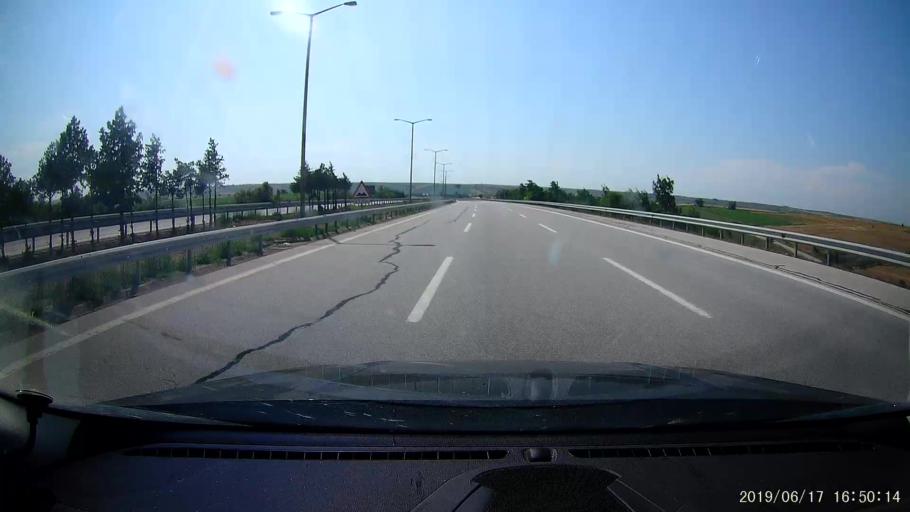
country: TR
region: Kirklareli
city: Babaeski
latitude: 41.5207
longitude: 27.0941
